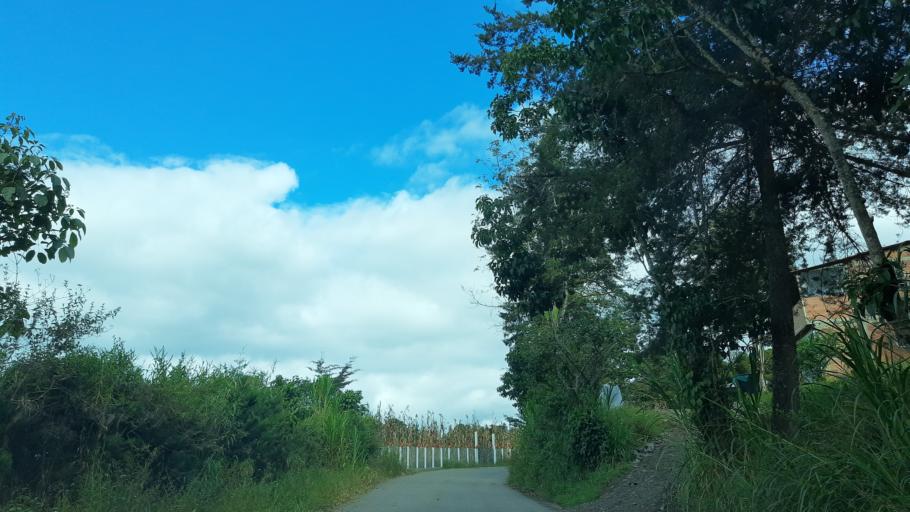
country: CO
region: Cundinamarca
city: Tenza
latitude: 5.0611
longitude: -73.4224
